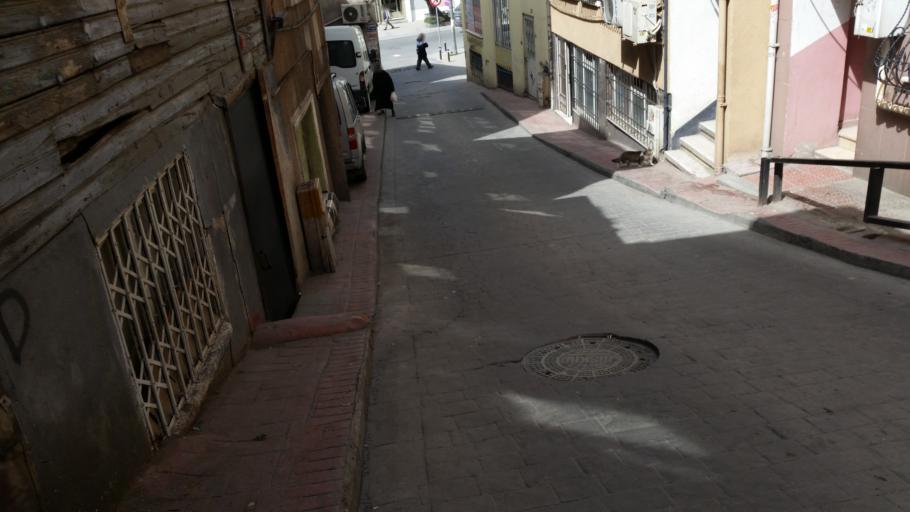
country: TR
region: Istanbul
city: Eminoenue
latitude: 41.0358
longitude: 28.9710
